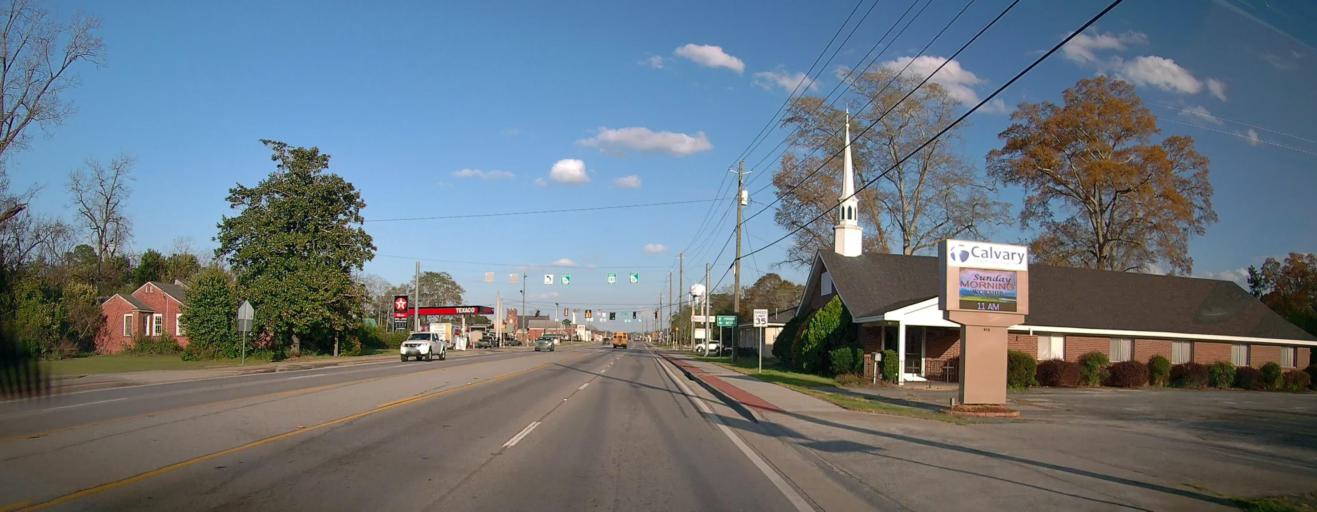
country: US
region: Georgia
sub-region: Evans County
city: Claxton
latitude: 32.1610
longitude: -81.9154
